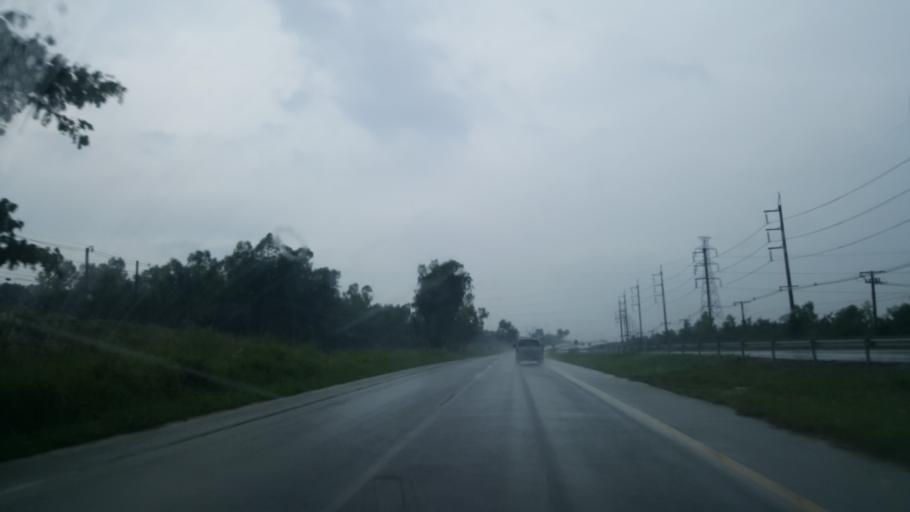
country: TH
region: Chon Buri
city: Ban Talat Bueng
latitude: 12.9320
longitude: 101.0367
